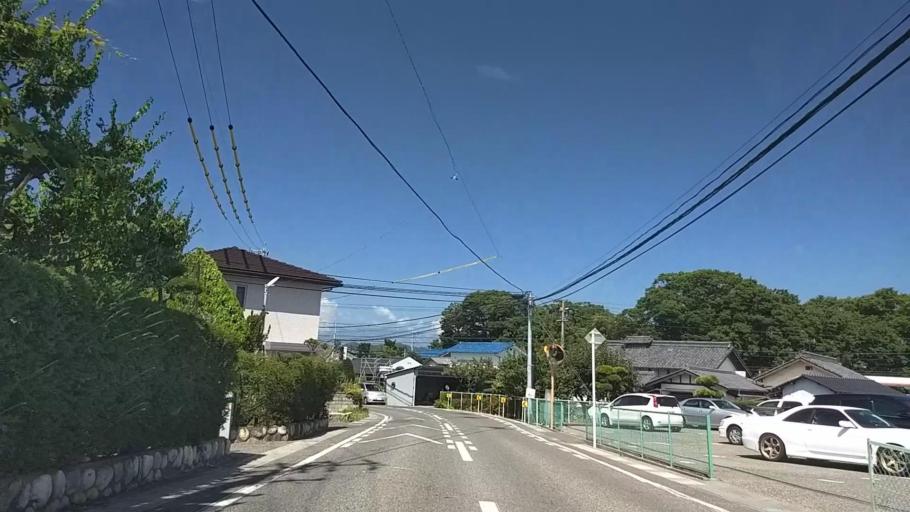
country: JP
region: Nagano
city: Matsumoto
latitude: 36.2374
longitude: 137.9916
